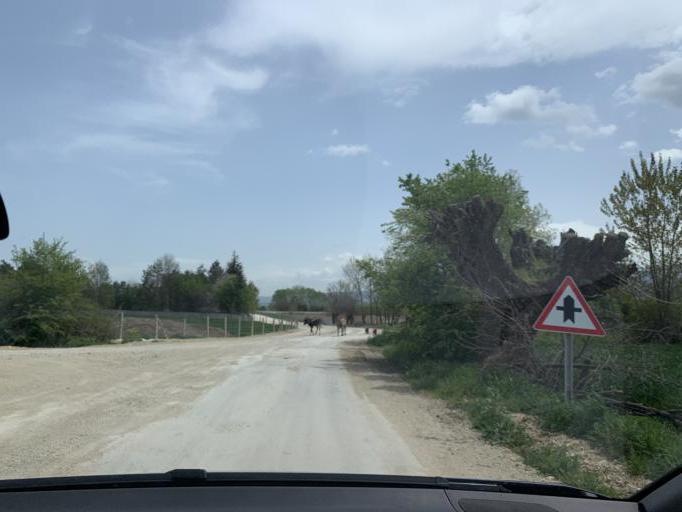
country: TR
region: Bolu
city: Bolu
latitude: 40.7596
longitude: 31.6912
